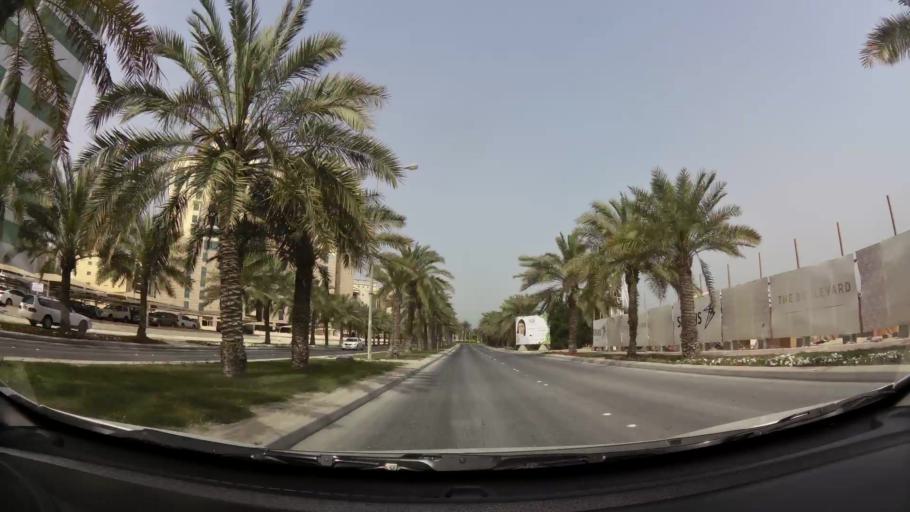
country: BH
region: Manama
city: Jidd Hafs
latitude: 26.2409
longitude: 50.5400
